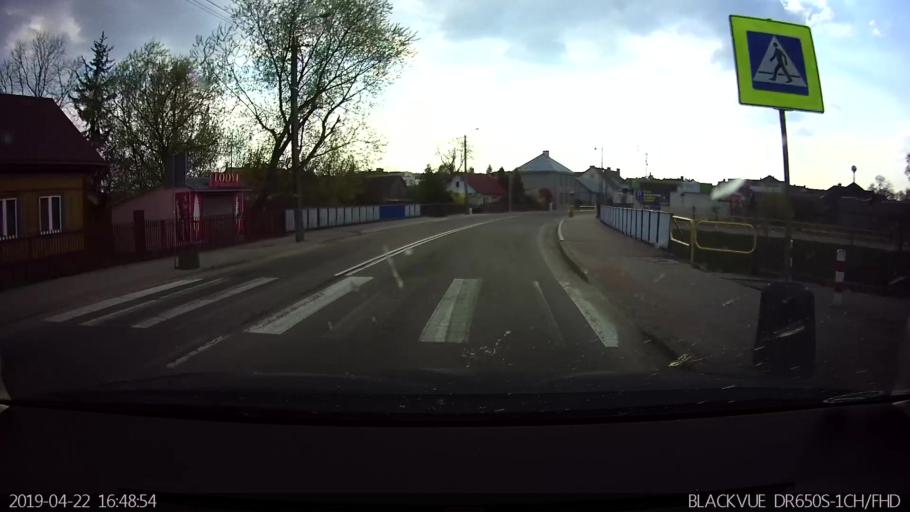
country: PL
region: Podlasie
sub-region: Powiat siemiatycki
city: Siemiatycze
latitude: 52.4272
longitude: 22.8691
